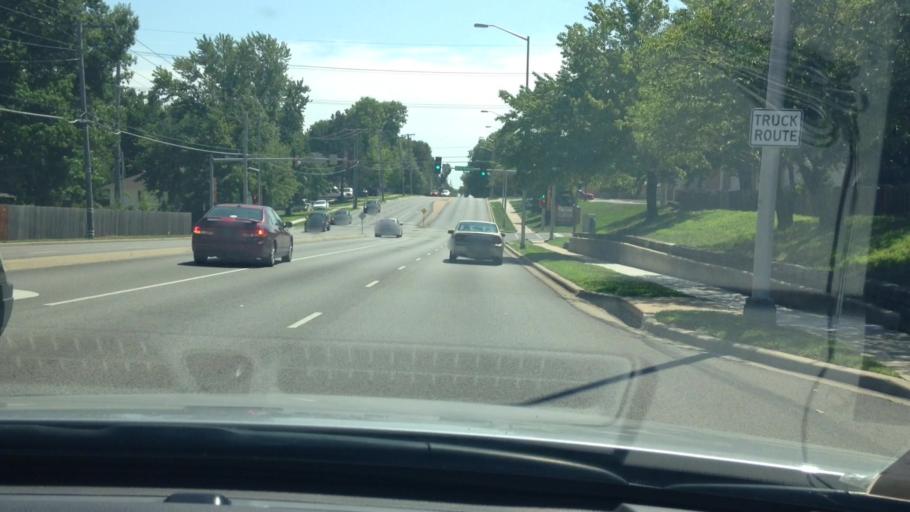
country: US
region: Kansas
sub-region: Johnson County
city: Overland Park
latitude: 38.9720
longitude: -94.6864
